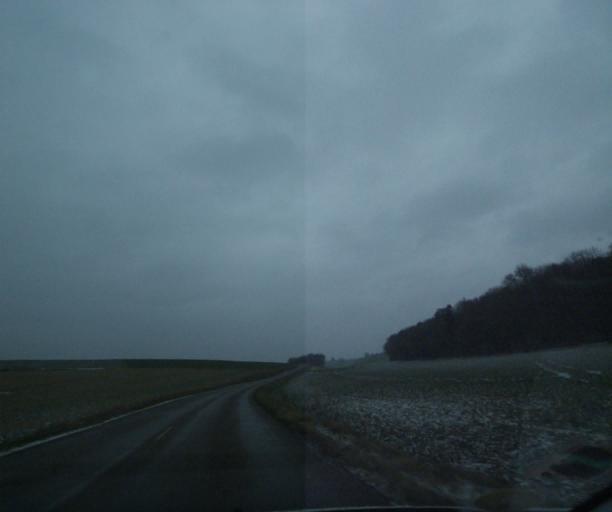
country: FR
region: Champagne-Ardenne
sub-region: Departement de la Haute-Marne
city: Wassy
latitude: 48.4344
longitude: 5.0235
